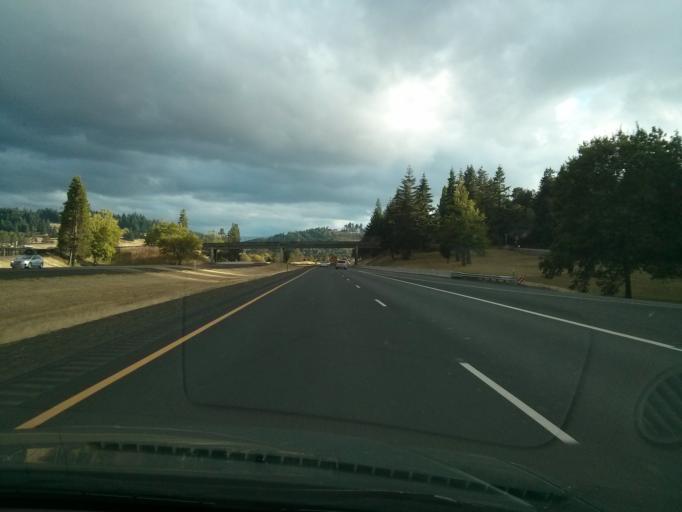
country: US
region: Oregon
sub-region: Douglas County
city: Yoncalla
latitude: 43.5150
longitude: -123.3149
